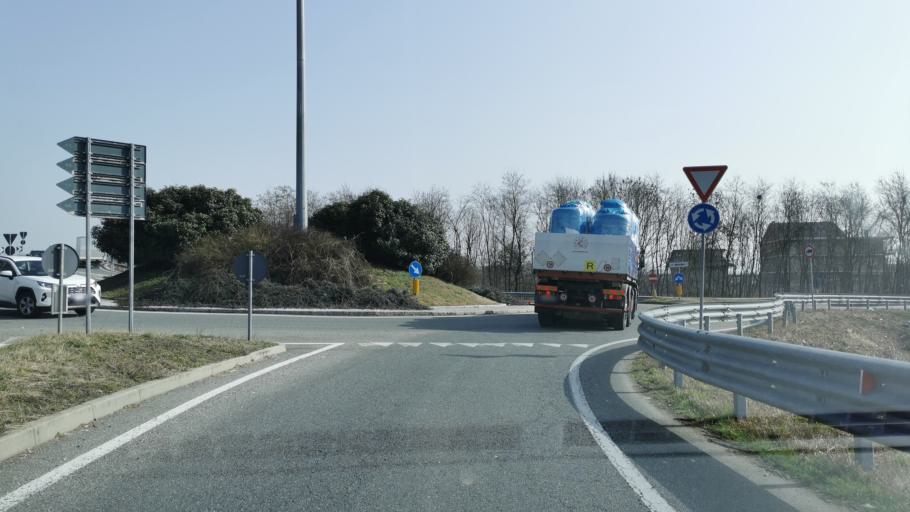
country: IT
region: Piedmont
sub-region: Provincia di Torino
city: Volpiano
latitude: 45.2109
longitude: 7.7796
